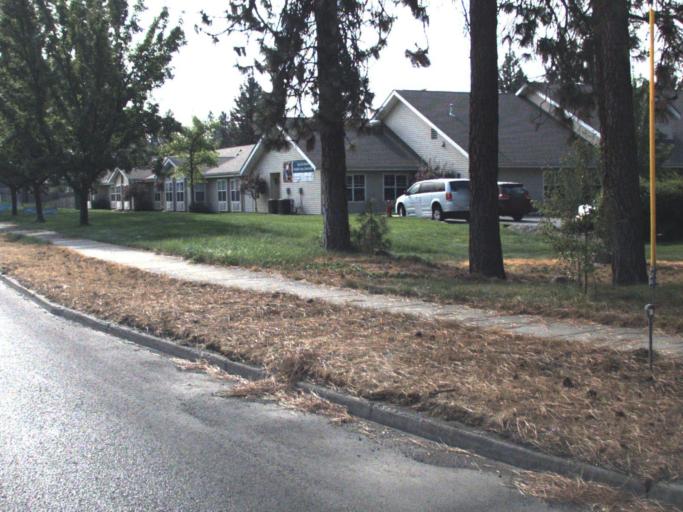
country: US
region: Washington
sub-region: Spokane County
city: Town and Country
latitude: 47.7258
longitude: -117.4953
